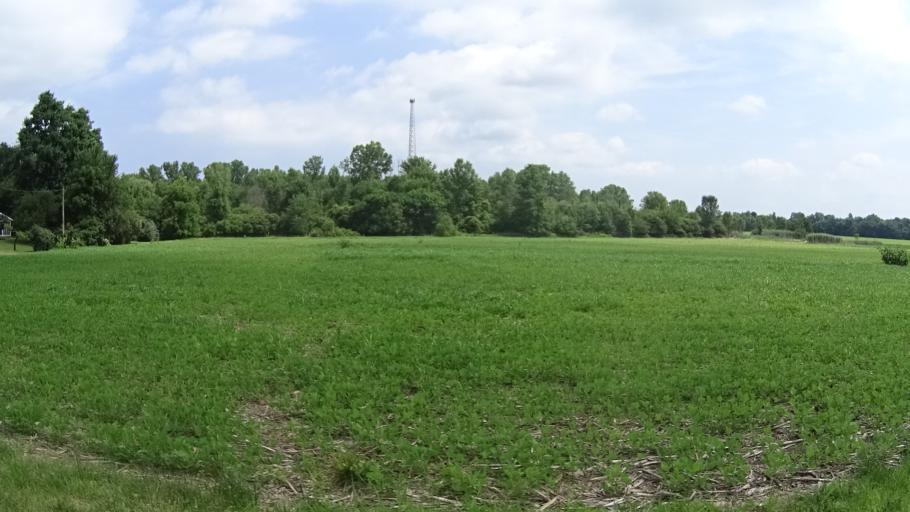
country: US
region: Ohio
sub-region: Lorain County
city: Vermilion
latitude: 41.3763
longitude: -82.3508
